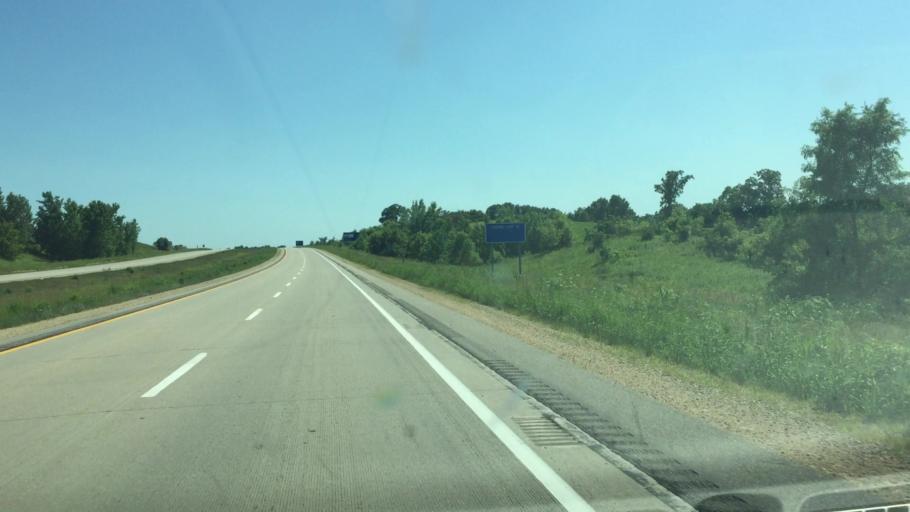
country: US
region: Iowa
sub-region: Jones County
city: Monticello
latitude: 42.2440
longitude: -91.1659
